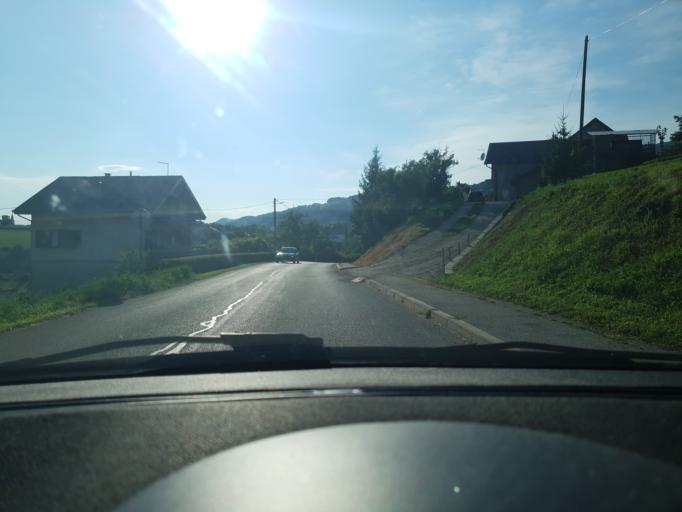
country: HR
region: Krapinsko-Zagorska
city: Radoboj
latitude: 46.1637
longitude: 15.9265
